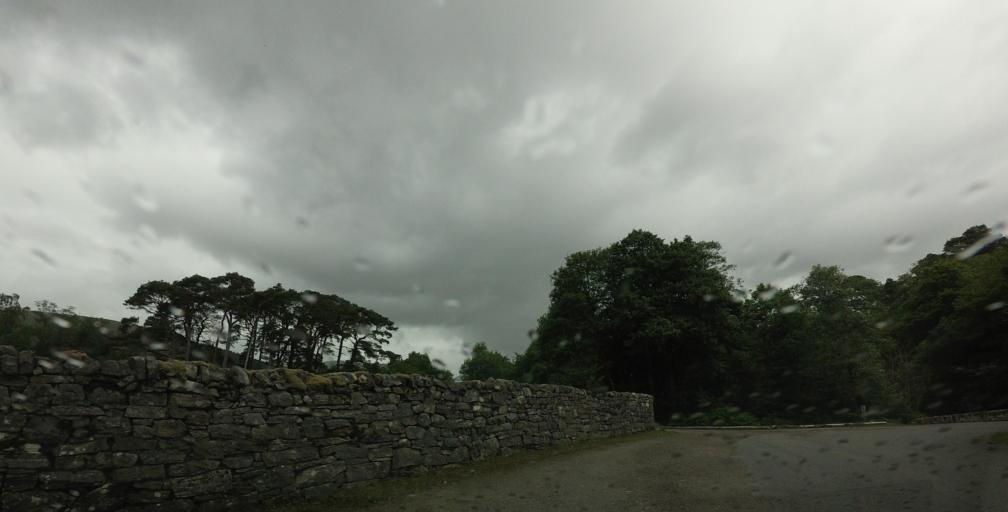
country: GB
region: Scotland
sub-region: Highland
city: Fort William
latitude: 56.8595
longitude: -5.2478
